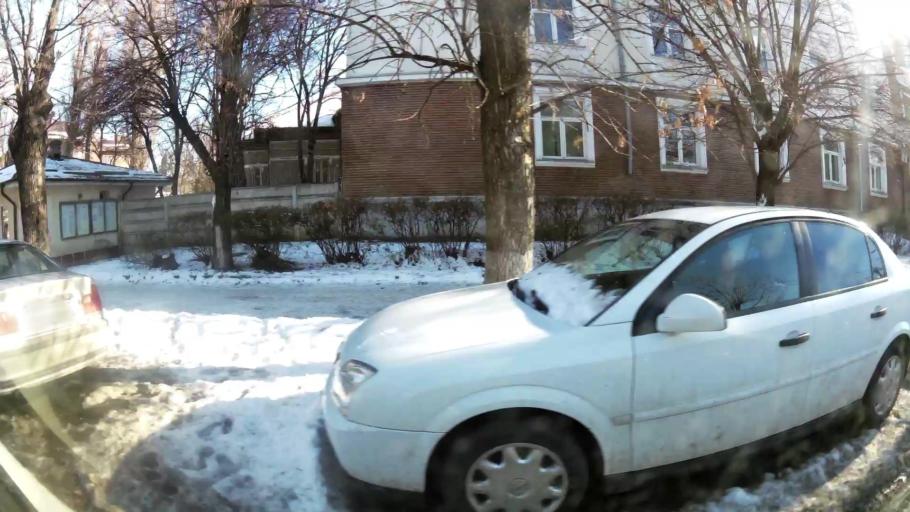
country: RO
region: Bucuresti
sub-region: Municipiul Bucuresti
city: Bucuresti
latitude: 44.4177
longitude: 26.0843
